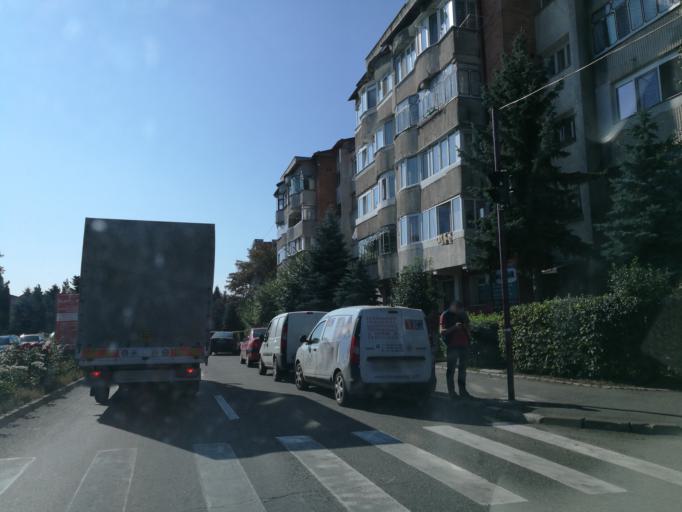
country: RO
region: Suceava
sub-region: Municipiul Falticeni
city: Falticeni
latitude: 47.4635
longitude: 26.3011
